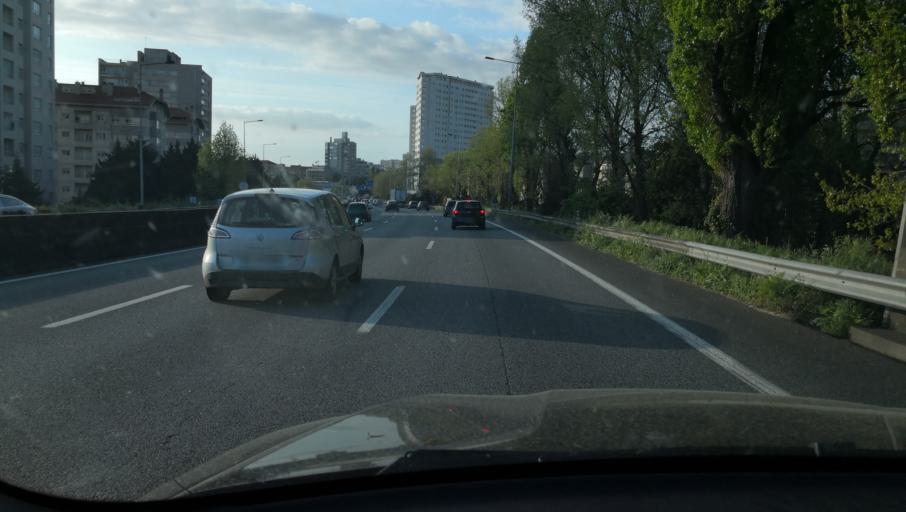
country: PT
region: Porto
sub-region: Matosinhos
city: Senhora da Hora
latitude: 41.1567
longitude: -8.6459
